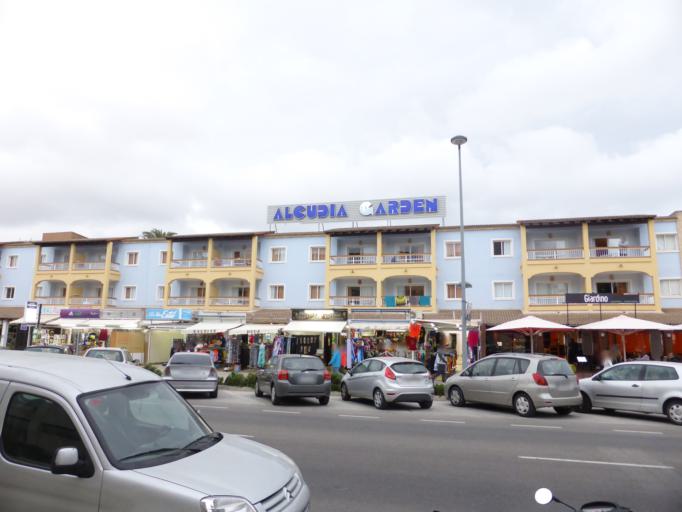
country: ES
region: Balearic Islands
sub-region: Illes Balears
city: Port d'Alcudia
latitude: 39.8412
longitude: 3.1279
